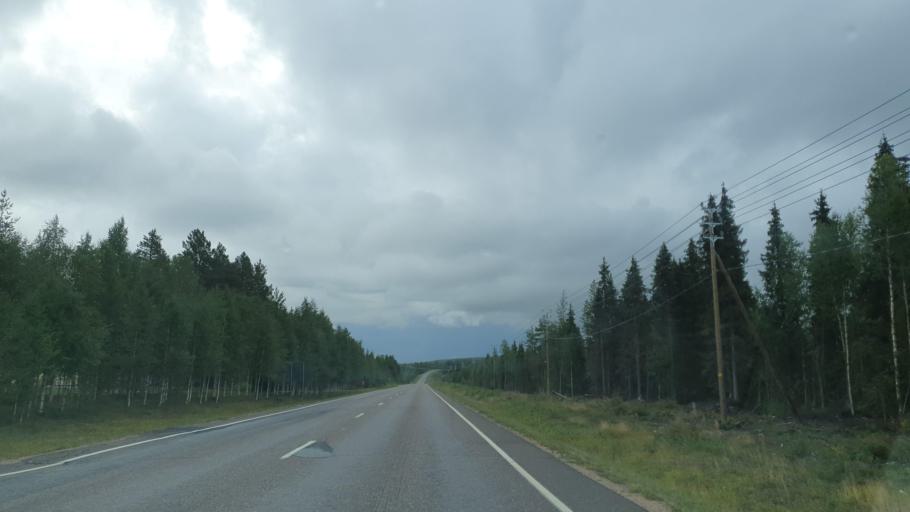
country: FI
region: Lapland
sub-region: Tunturi-Lappi
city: Kolari
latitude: 67.2035
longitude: 23.9110
